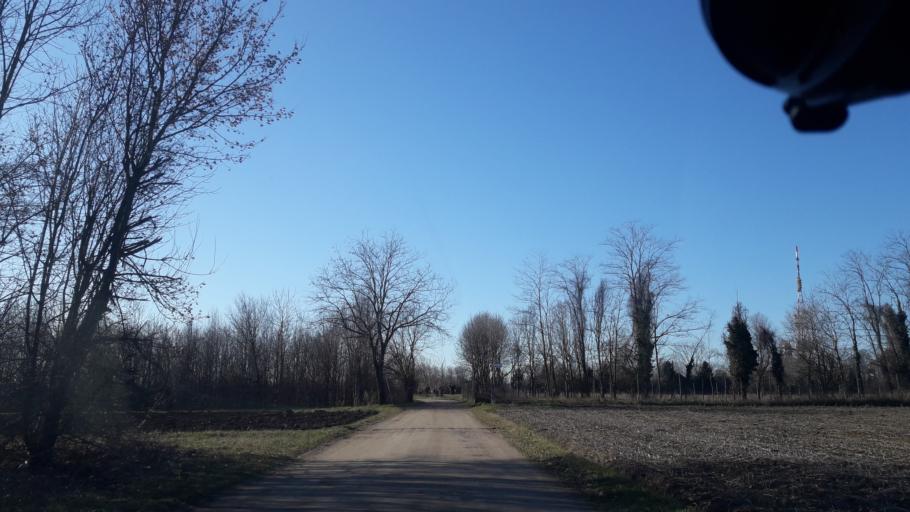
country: IT
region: Friuli Venezia Giulia
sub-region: Provincia di Udine
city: Udine
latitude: 46.0401
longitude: 13.2655
